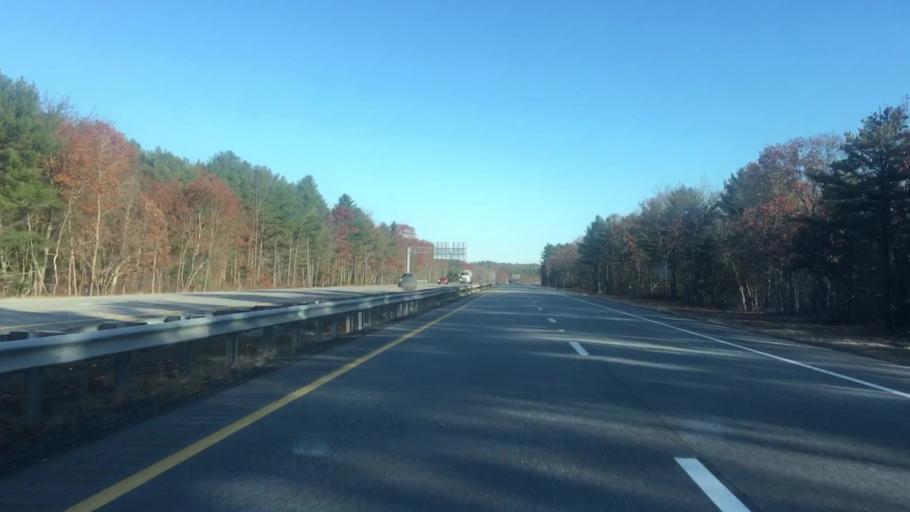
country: US
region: Maine
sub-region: Cumberland County
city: New Gloucester
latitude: 43.9439
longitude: -70.3334
